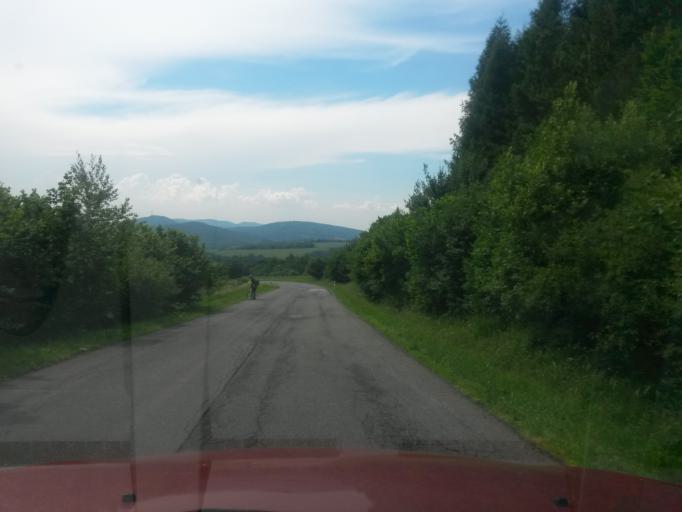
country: SK
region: Presovsky
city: Snina
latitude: 48.9847
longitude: 22.2832
